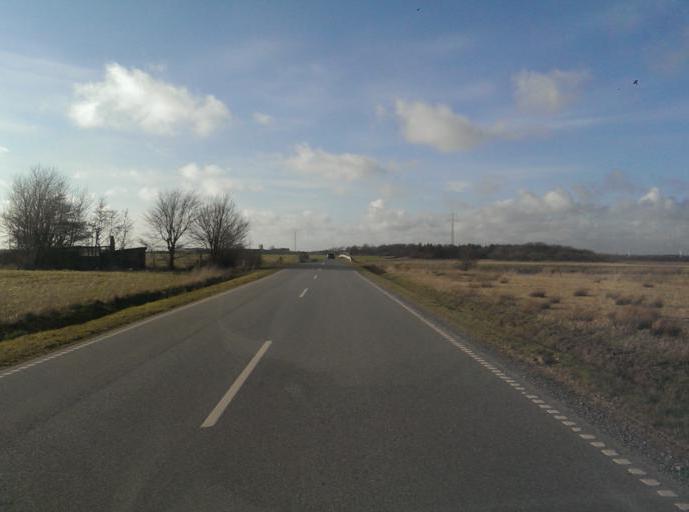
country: DK
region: South Denmark
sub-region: Esbjerg Kommune
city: Tjaereborg
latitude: 55.4412
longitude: 8.6241
